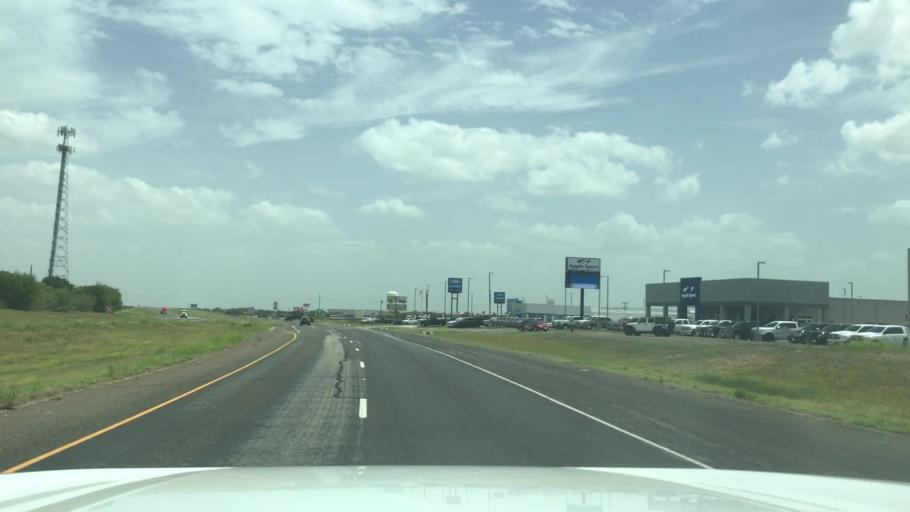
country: US
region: Texas
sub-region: Falls County
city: Marlin
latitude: 31.3265
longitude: -96.8881
